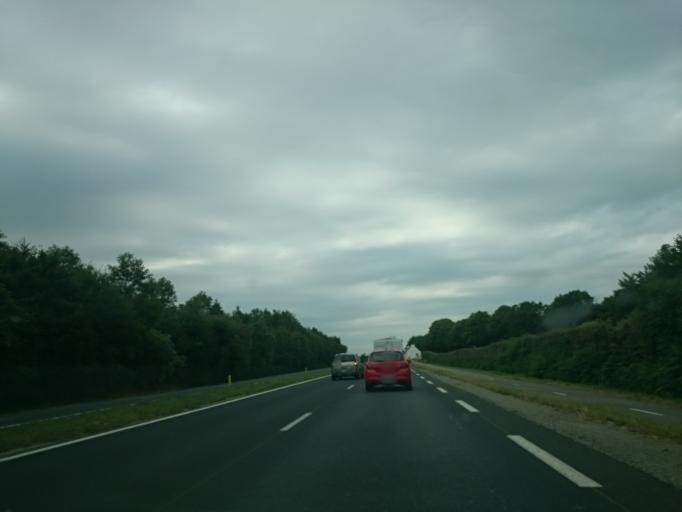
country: FR
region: Brittany
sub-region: Departement du Finistere
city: Guilers
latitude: 48.4146
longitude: -4.5432
